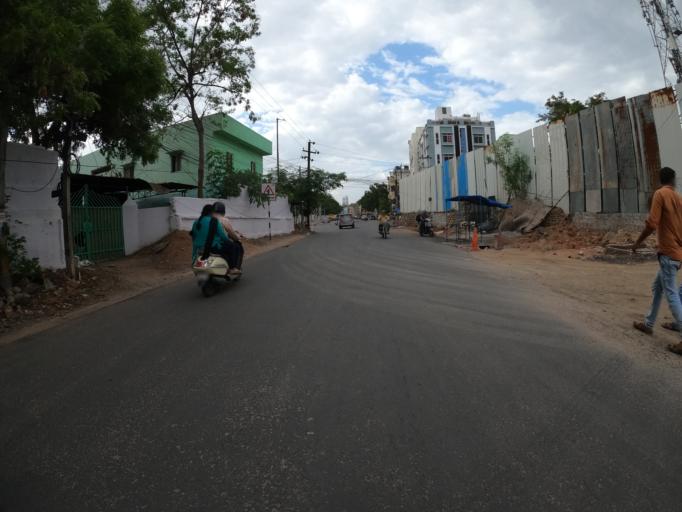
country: IN
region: Telangana
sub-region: Hyderabad
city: Hyderabad
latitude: 17.4105
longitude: 78.3949
